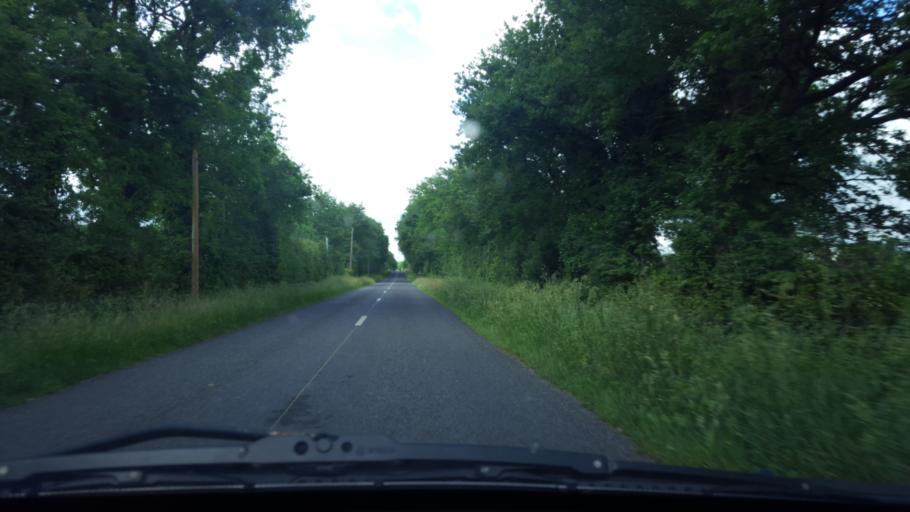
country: FR
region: Pays de la Loire
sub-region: Departement de la Loire-Atlantique
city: Saint-Lumine-de-Coutais
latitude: 47.0143
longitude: -1.7354
